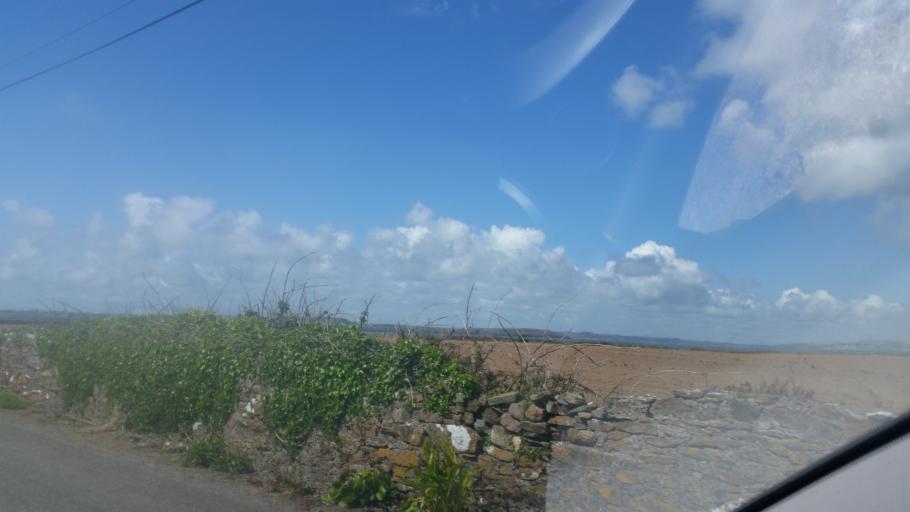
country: IE
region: Munster
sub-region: Waterford
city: Dunmore East
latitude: 52.1363
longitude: -6.9203
